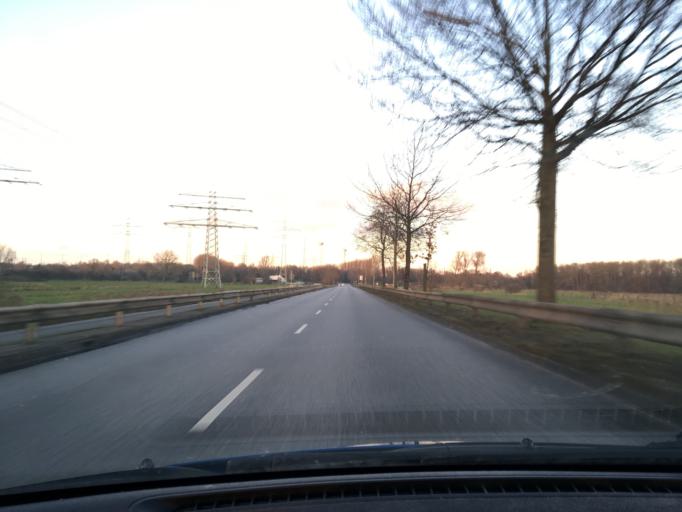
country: DE
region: Hamburg
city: Altona
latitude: 53.4901
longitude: 9.9070
